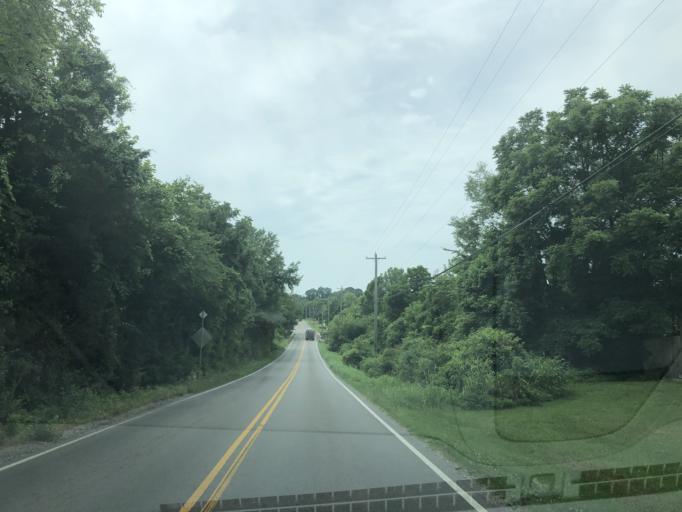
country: US
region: Tennessee
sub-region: Williamson County
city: Nolensville
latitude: 36.0224
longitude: -86.6806
